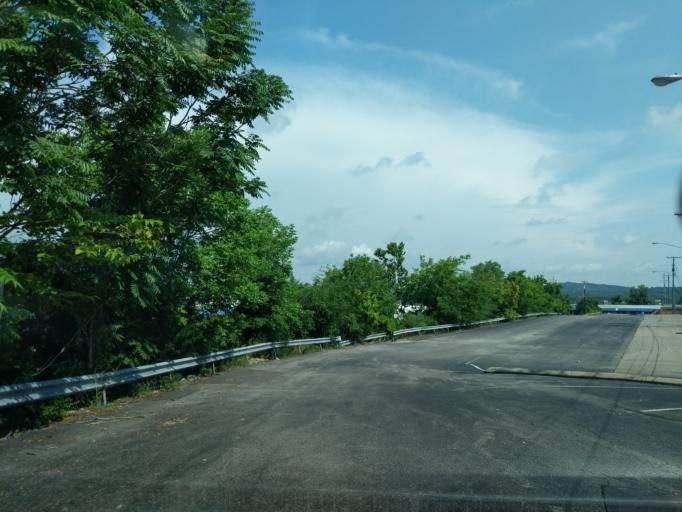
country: US
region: Tennessee
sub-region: Davidson County
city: Goodlettsville
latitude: 36.3145
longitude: -86.7044
